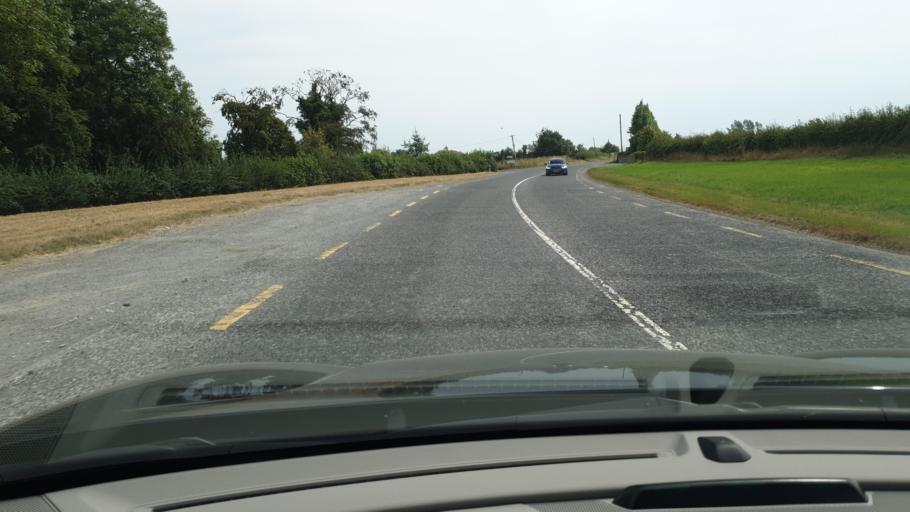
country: IE
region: Leinster
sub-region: An Mhi
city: Navan
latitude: 53.6427
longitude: -6.6217
